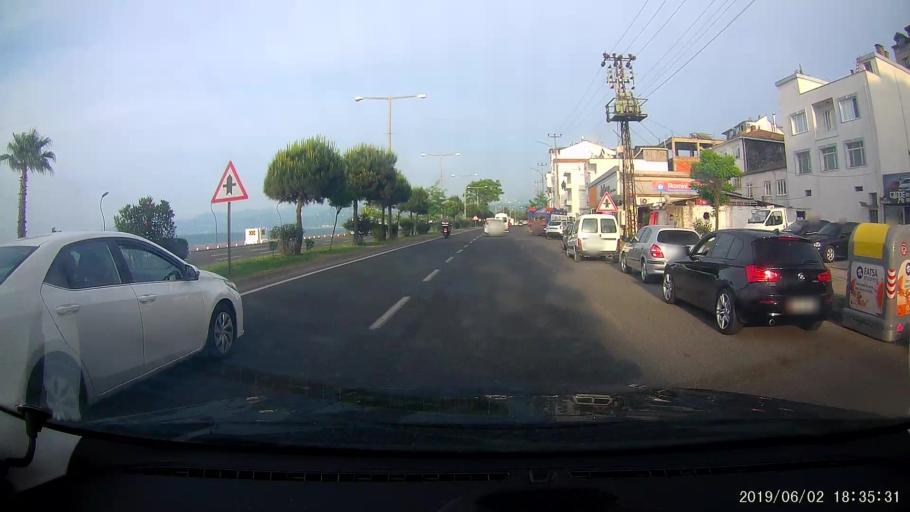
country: TR
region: Ordu
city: Fatsa
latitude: 41.0262
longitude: 37.5176
